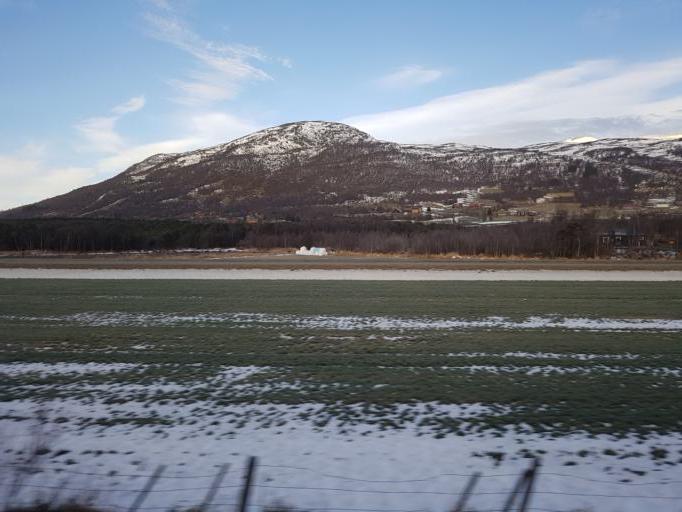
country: NO
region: Sor-Trondelag
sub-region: Oppdal
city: Oppdal
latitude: 62.6028
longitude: 9.7178
